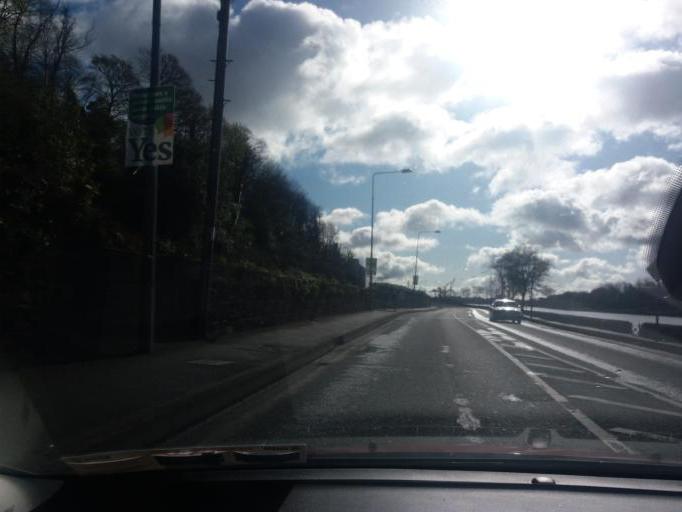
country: IE
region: Munster
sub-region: County Cork
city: Cork
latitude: 51.9027
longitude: -8.4390
